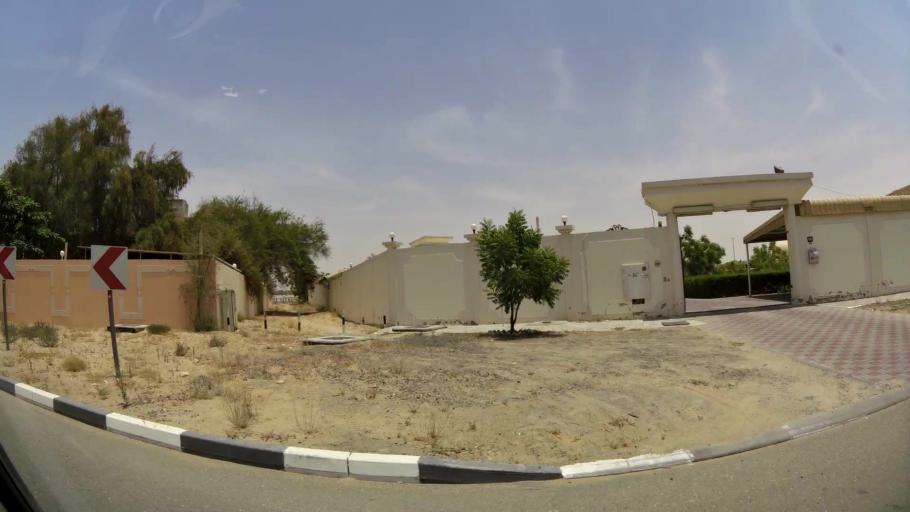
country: AE
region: Ash Shariqah
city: Sharjah
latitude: 25.2311
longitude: 55.4643
